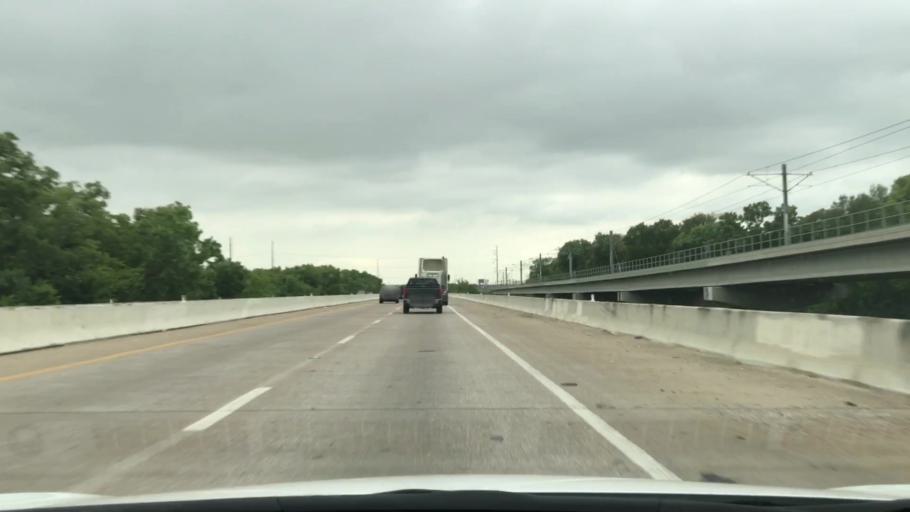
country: US
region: Texas
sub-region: Dallas County
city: Irving
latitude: 32.8510
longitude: -96.8891
